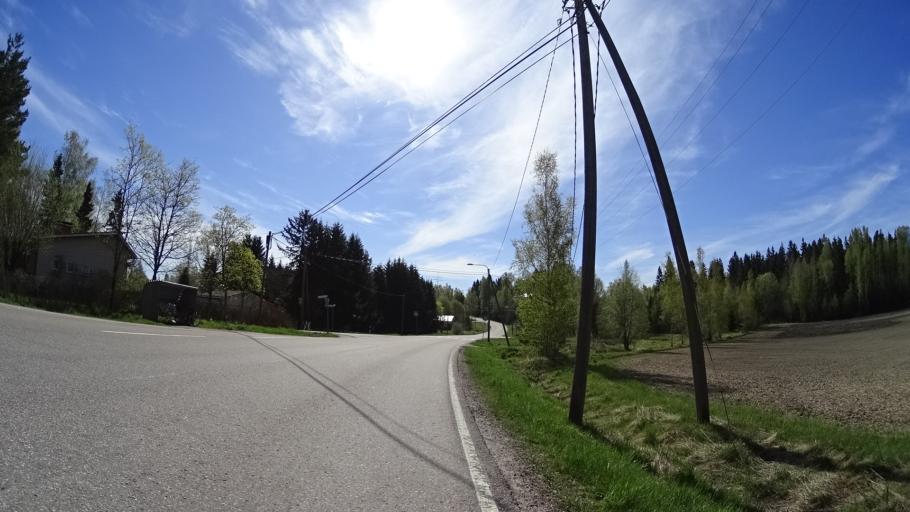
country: FI
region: Uusimaa
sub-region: Helsinki
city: Nurmijaervi
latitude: 60.3662
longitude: 24.8472
